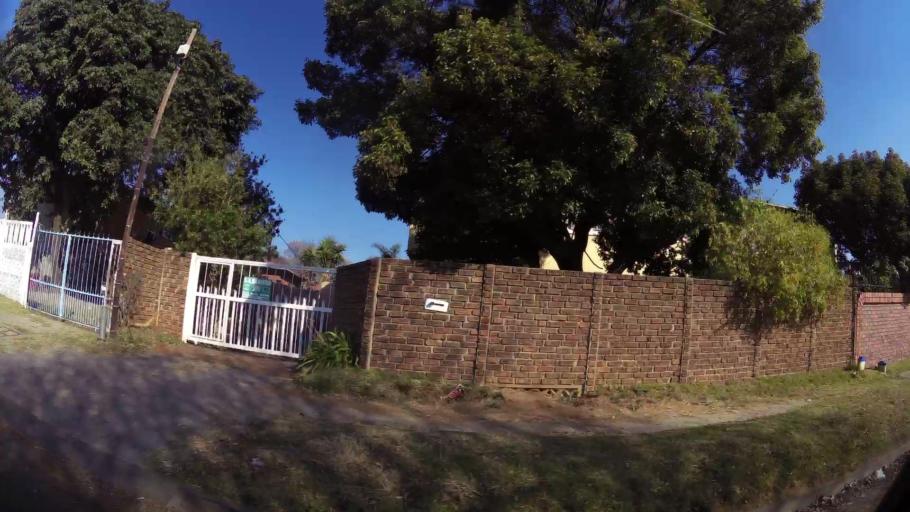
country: ZA
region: Gauteng
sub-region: City of Johannesburg Metropolitan Municipality
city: Johannesburg
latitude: -26.2494
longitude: 28.0058
